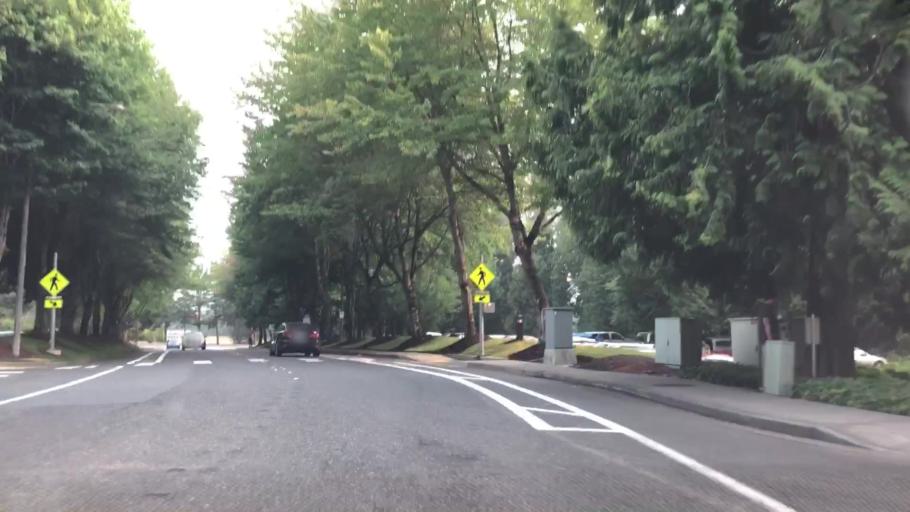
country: US
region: Washington
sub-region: King County
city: Redmond
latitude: 47.6534
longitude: -122.1409
